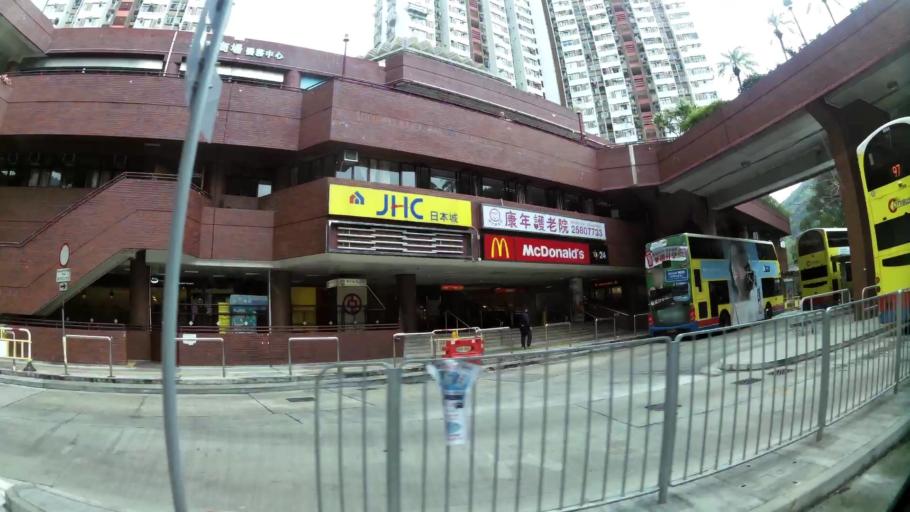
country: HK
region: Central and Western
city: Central
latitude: 22.2412
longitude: 114.1564
